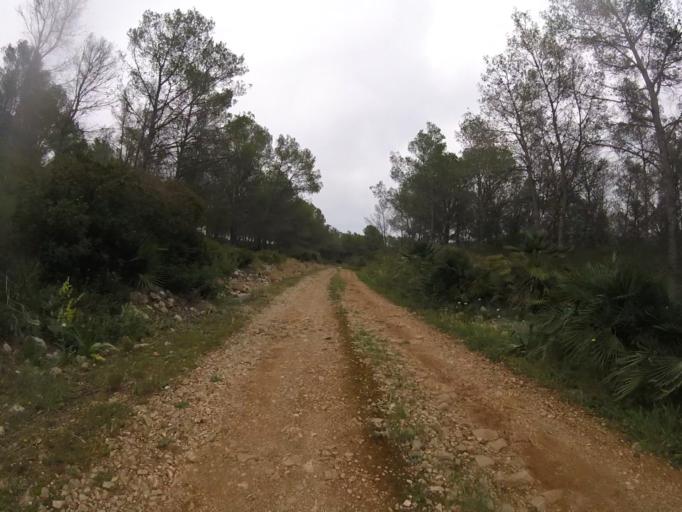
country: ES
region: Valencia
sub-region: Provincia de Castello
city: Alcala de Xivert
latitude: 40.3176
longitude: 0.2705
